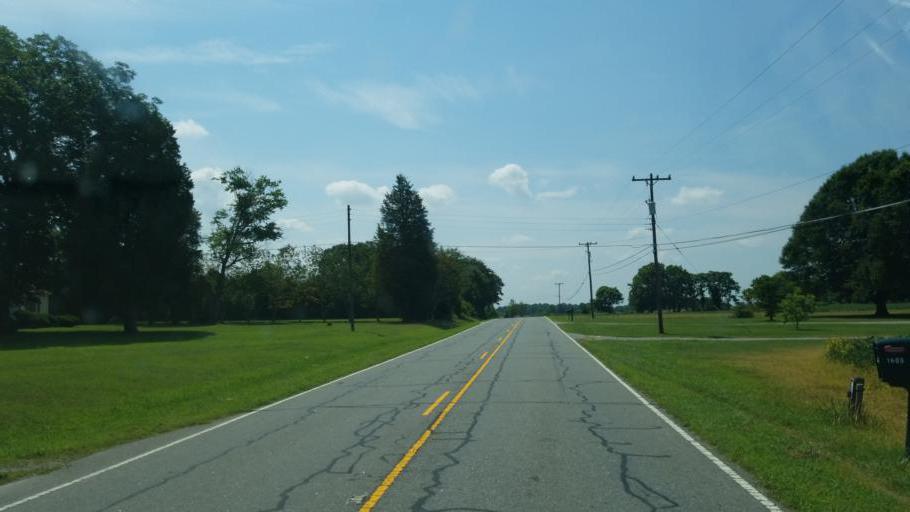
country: US
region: North Carolina
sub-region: Gaston County
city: Cherryville
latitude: 35.4707
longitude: -81.4413
